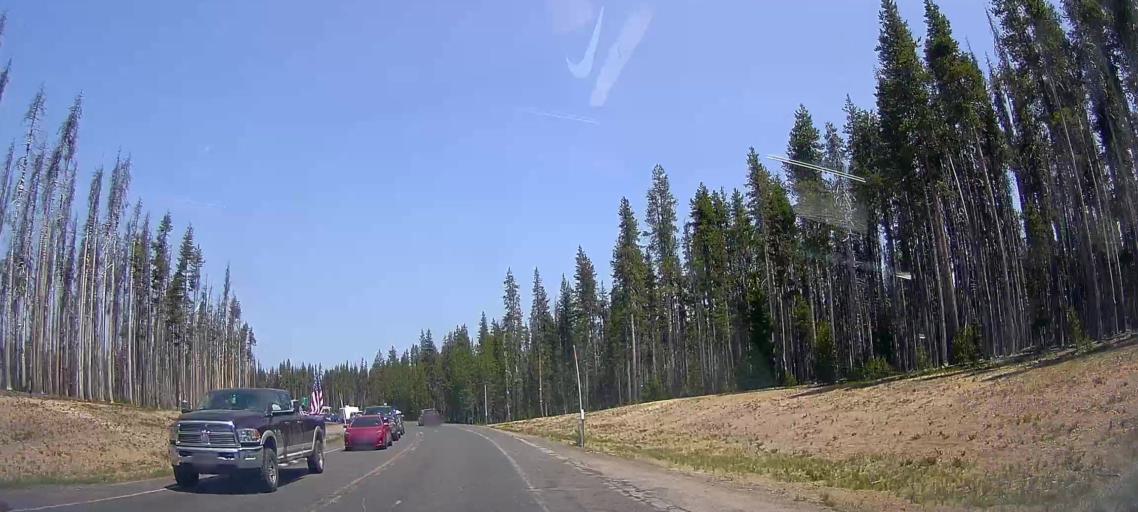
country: US
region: Oregon
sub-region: Lane County
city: Oakridge
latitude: 43.0868
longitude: -122.1164
